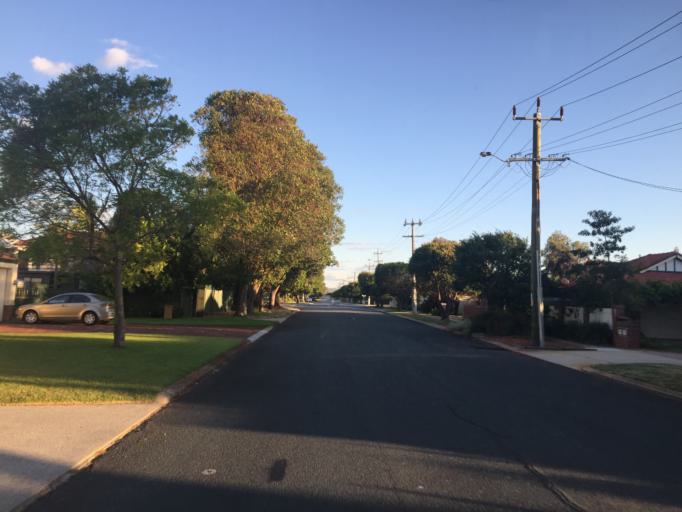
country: AU
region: Western Australia
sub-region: Belmont
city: Rivervale
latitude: -31.9614
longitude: 115.9218
